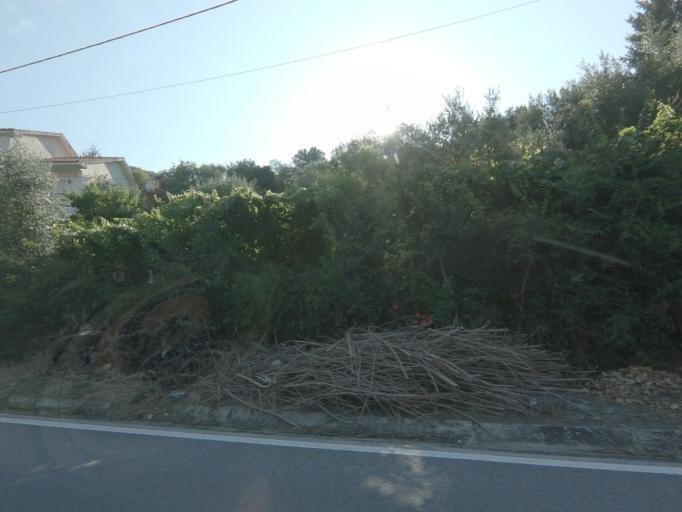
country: PT
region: Viseu
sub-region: Tabuaco
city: Tabuaco
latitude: 41.1426
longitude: -7.5739
